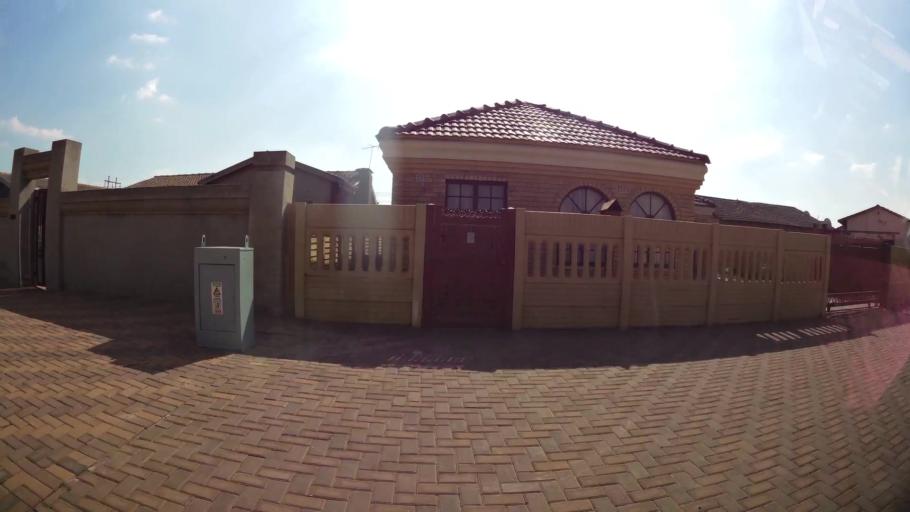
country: ZA
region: Gauteng
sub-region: Ekurhuleni Metropolitan Municipality
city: Benoni
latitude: -26.1416
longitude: 28.4082
